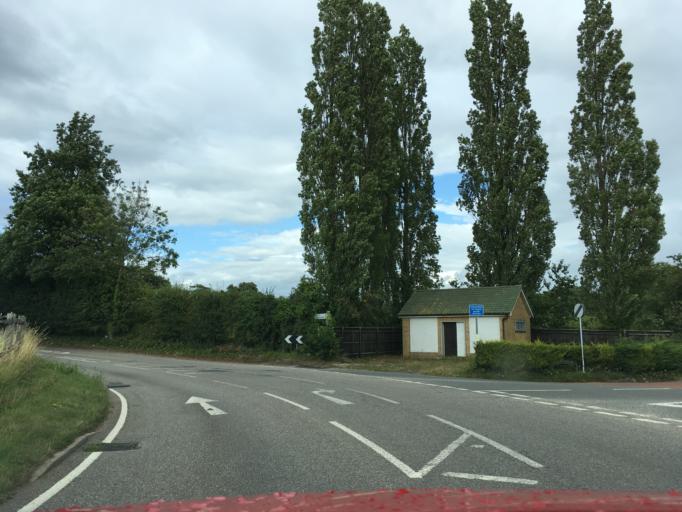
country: GB
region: England
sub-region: Kent
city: Maidstone
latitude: 51.2415
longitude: 0.4915
